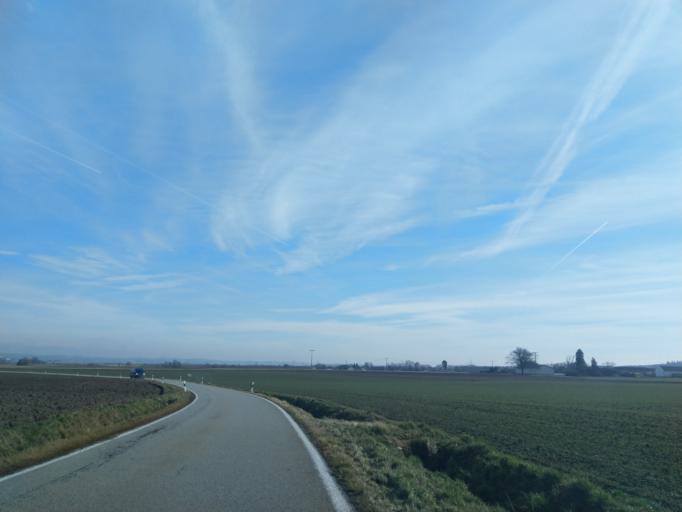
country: DE
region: Bavaria
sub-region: Lower Bavaria
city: Buchhofen
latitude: 48.6704
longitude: 12.9316
